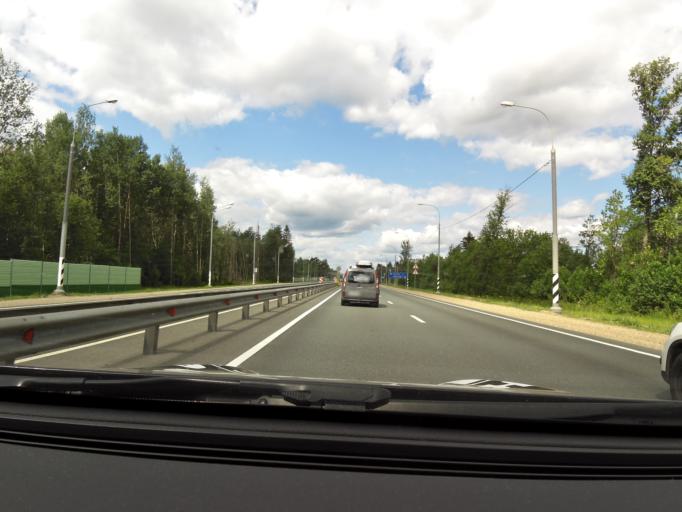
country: RU
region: Tverskaya
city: Torzhok
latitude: 57.0180
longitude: 35.0620
